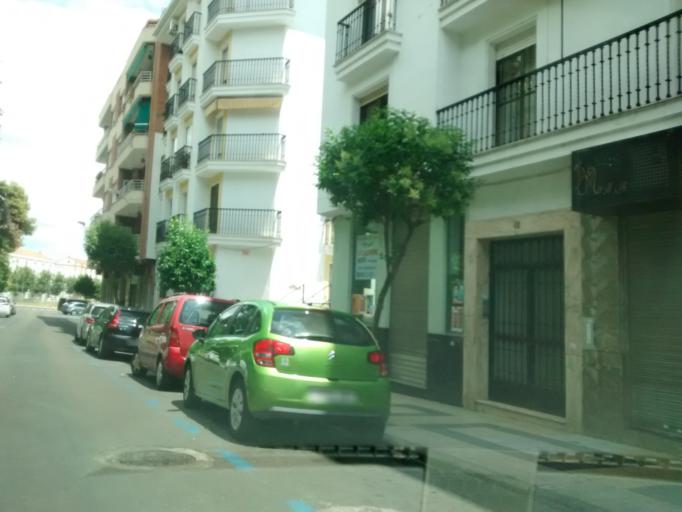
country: ES
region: Extremadura
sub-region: Provincia de Badajoz
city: Merida
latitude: 38.9193
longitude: -6.3406
